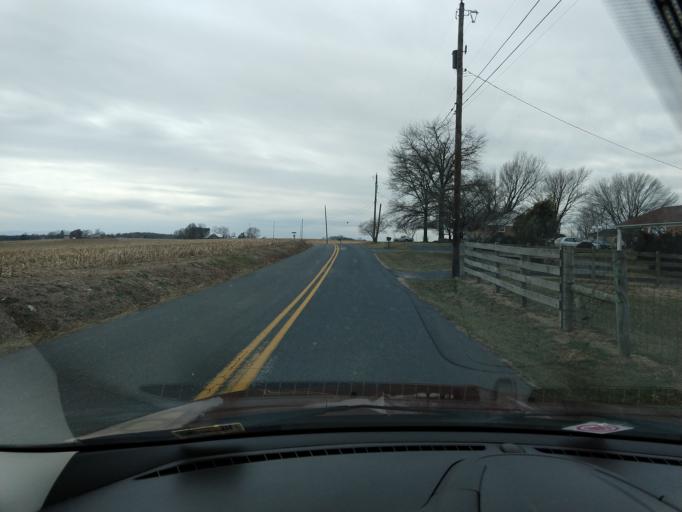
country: US
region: Virginia
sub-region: Augusta County
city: Weyers Cave
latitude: 38.2171
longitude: -78.8978
